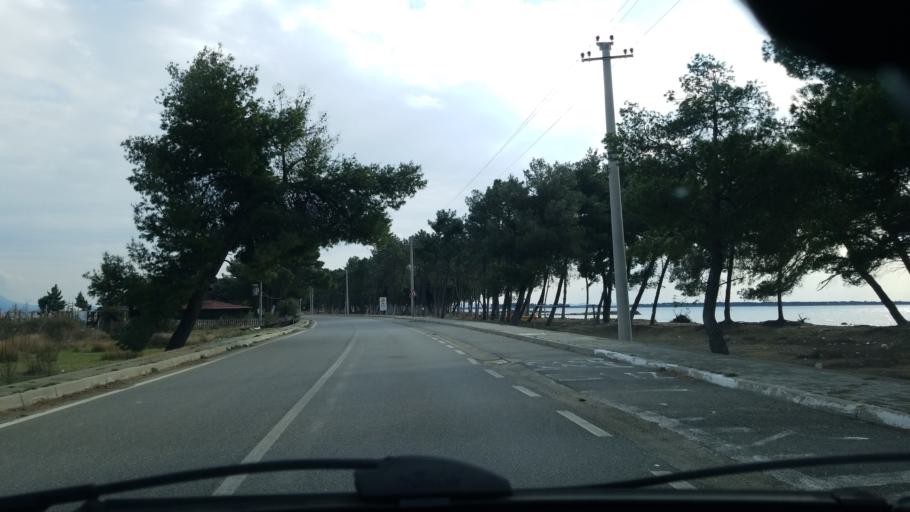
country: AL
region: Lezhe
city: Shengjin
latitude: 41.7886
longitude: 19.6031
